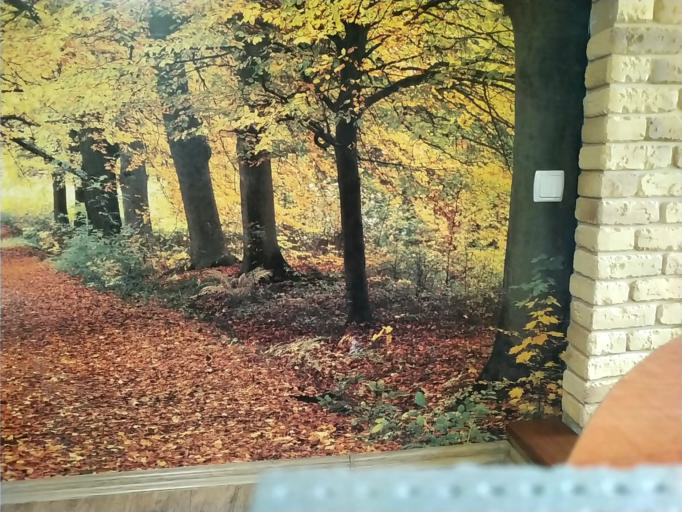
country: RU
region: Tverskaya
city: Staritsa
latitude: 56.5062
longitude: 35.1678
